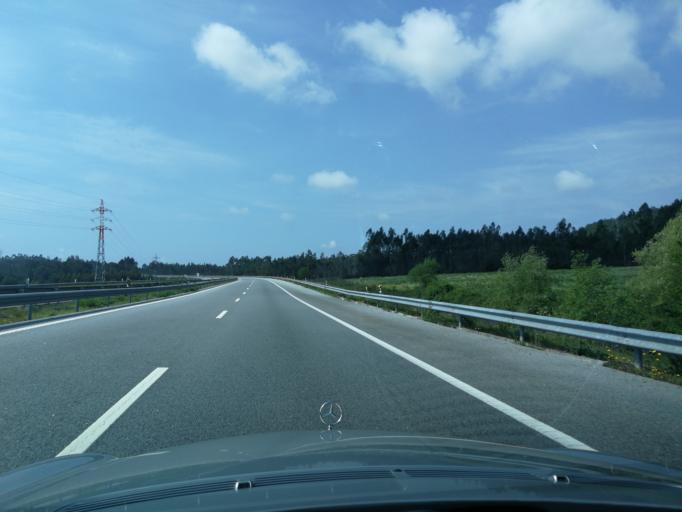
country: PT
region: Braga
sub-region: Vila Nova de Famalicao
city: Ribeirao
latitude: 41.3890
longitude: -8.5865
